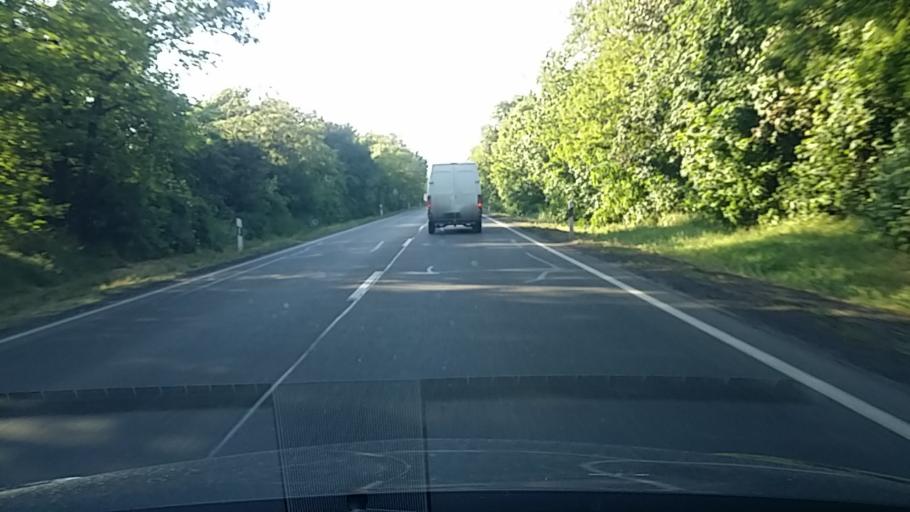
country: HU
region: Fejer
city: dunaujvaros
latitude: 46.9364
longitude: 18.9226
